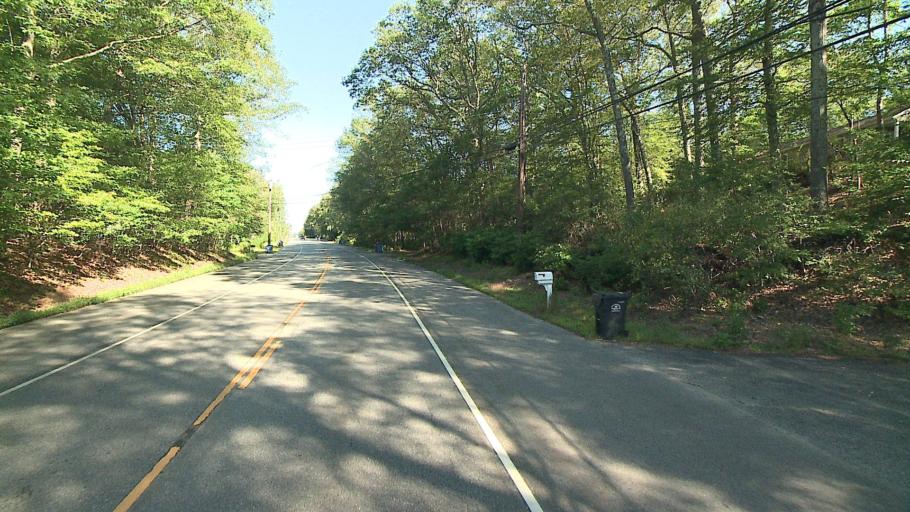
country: US
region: Connecticut
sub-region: New London County
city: Gales Ferry
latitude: 41.4153
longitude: -72.0739
